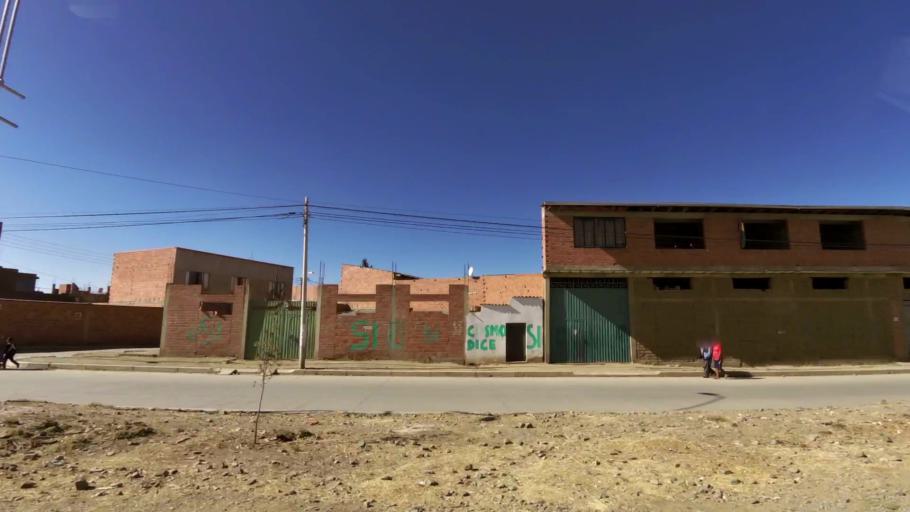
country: BO
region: La Paz
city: La Paz
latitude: -16.5274
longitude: -68.2274
